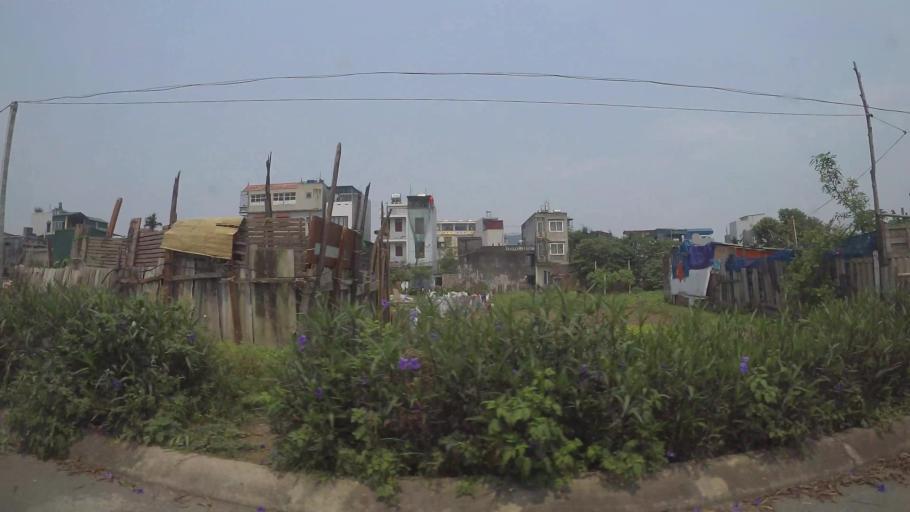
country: VN
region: Ha Noi
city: Van Dien
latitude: 20.9487
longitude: 105.8395
